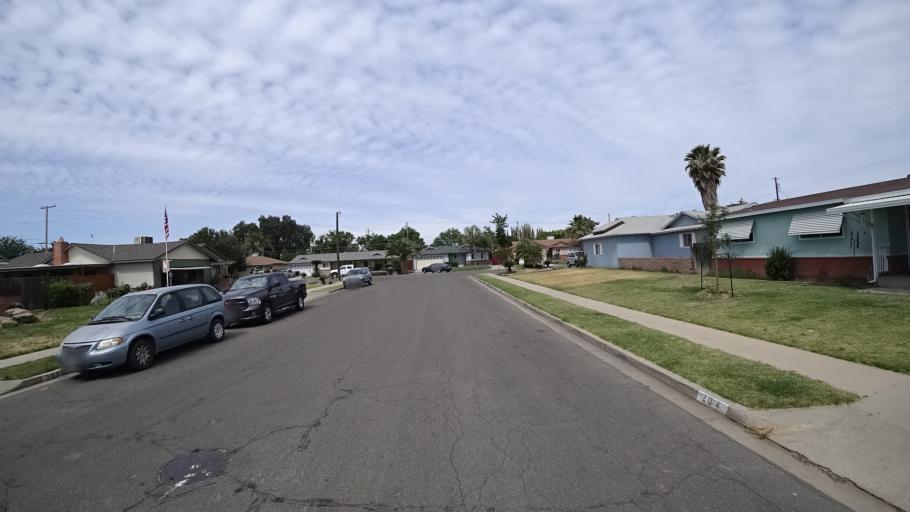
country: US
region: California
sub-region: Kings County
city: Hanford
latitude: 36.3486
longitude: -119.6444
